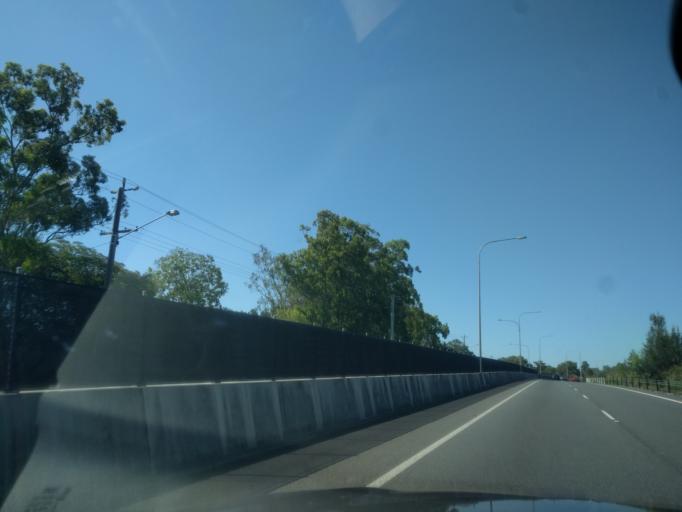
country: AU
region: Queensland
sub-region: Logan
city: Park Ridge South
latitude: -27.7163
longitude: 153.0332
